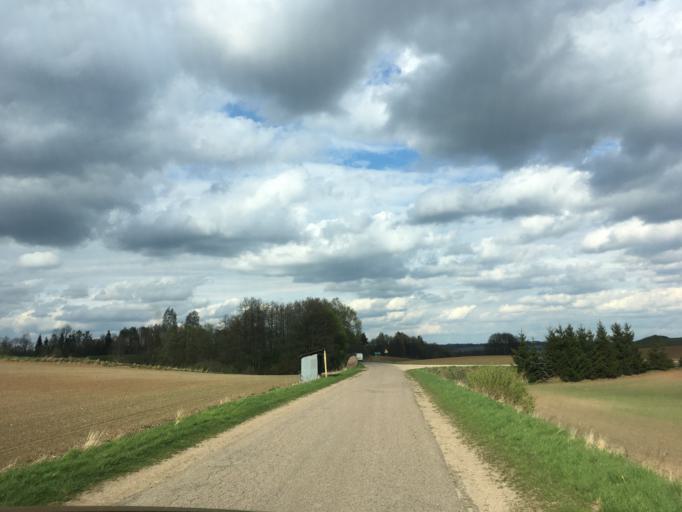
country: PL
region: Podlasie
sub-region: Suwalki
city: Suwalki
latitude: 54.3710
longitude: 22.9287
